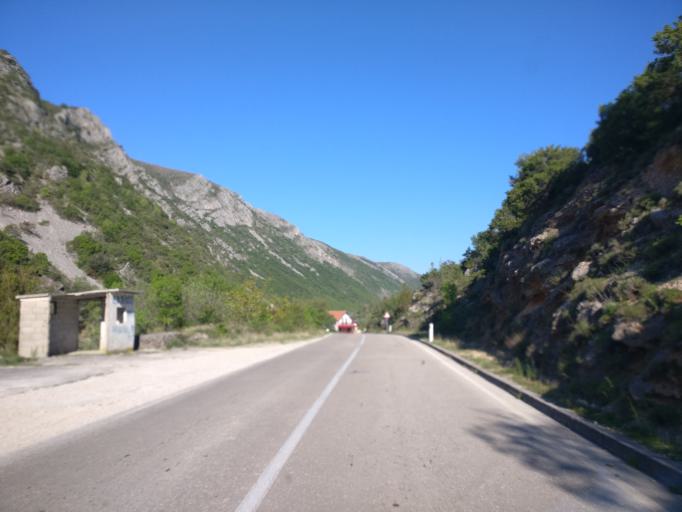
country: BA
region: Federation of Bosnia and Herzegovina
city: Stolac
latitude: 43.0765
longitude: 18.0249
